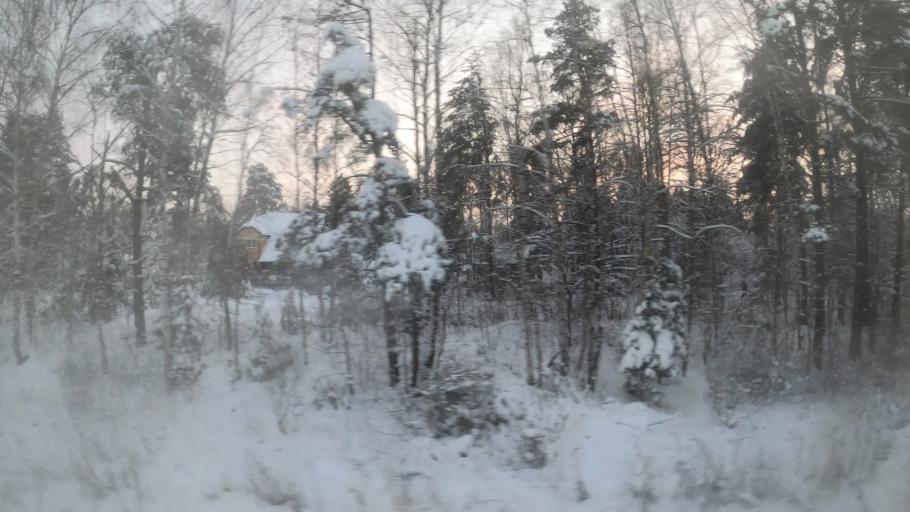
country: RU
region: Moskovskaya
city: Nekrasovskiy
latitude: 56.0787
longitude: 37.4981
